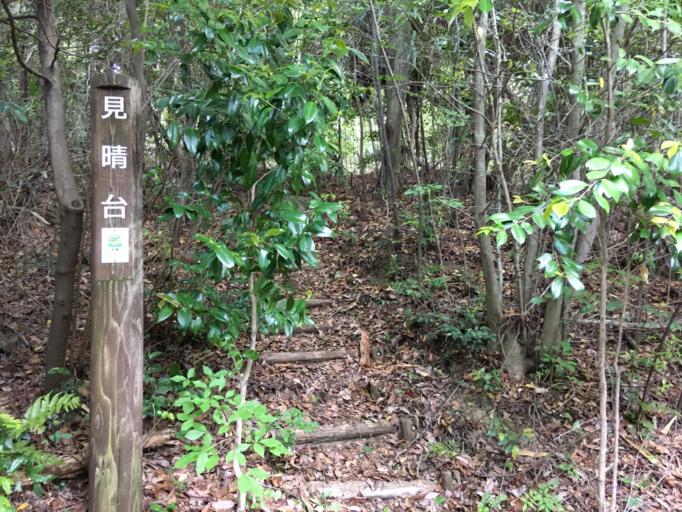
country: JP
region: Nara
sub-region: Ikoma-shi
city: Ikoma
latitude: 34.7024
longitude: 135.7122
